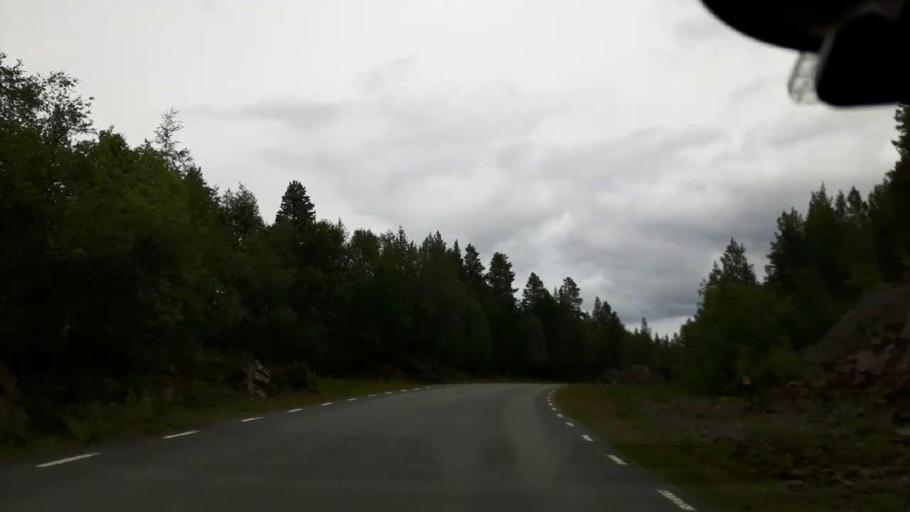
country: SE
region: Jaemtland
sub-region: Krokoms Kommun
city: Valla
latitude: 63.6578
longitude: 13.8300
